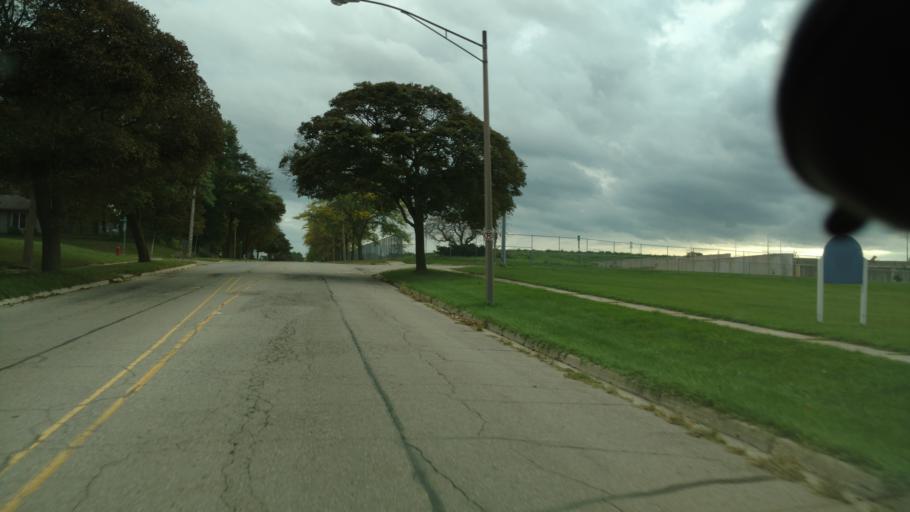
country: US
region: Michigan
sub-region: Ingham County
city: Edgemont Park
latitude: 42.7393
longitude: -84.5771
